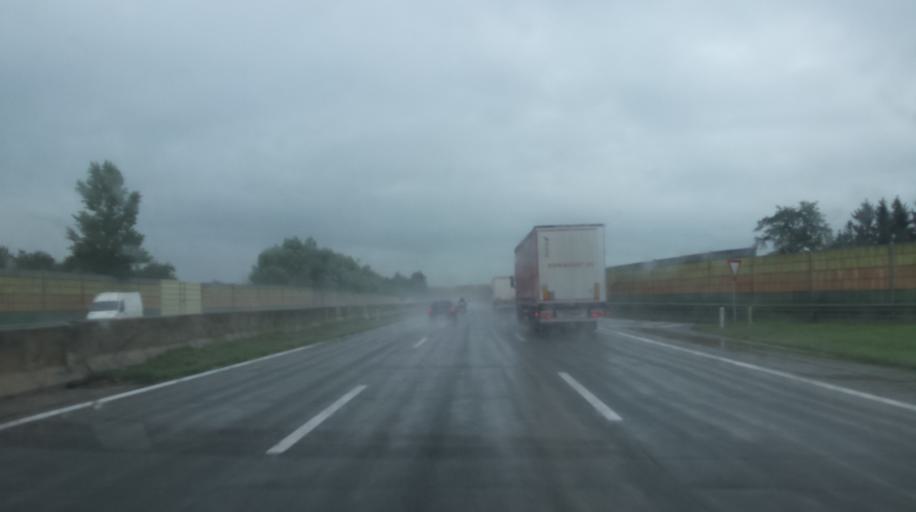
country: AT
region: Lower Austria
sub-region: Politischer Bezirk Amstetten
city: Haag
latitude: 48.1384
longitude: 14.5813
